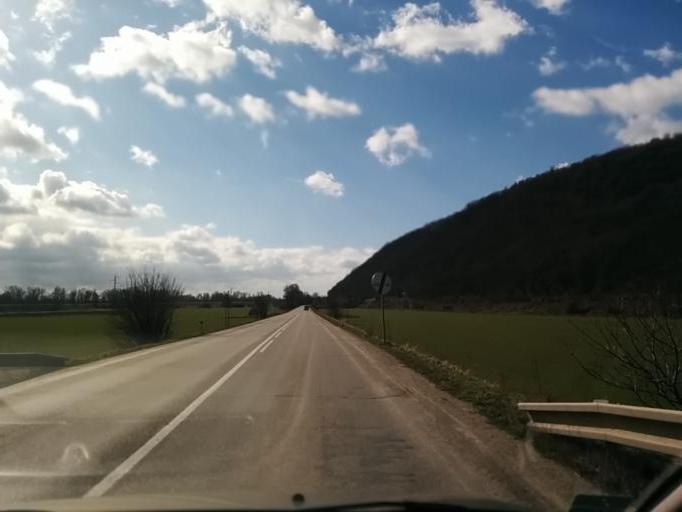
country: SK
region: Trenciansky
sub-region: Okres Nove Mesto nad Vahom
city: Nove Mesto nad Vahom
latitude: 48.7906
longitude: 17.8674
